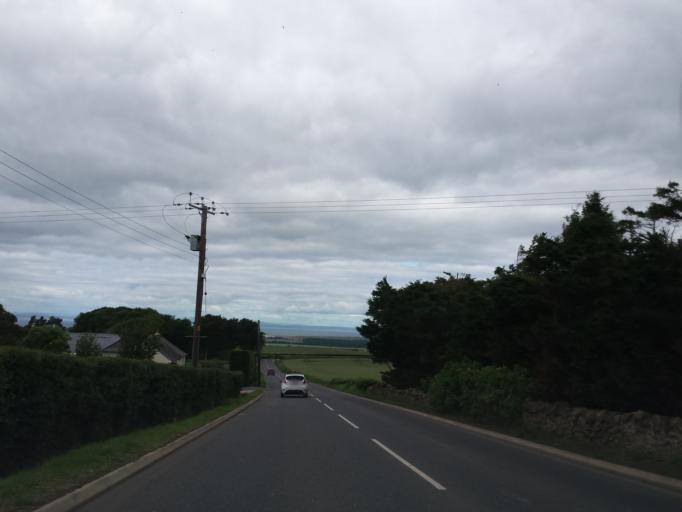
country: GB
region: Scotland
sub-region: East Lothian
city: Haddington
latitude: 55.9740
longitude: -2.8039
